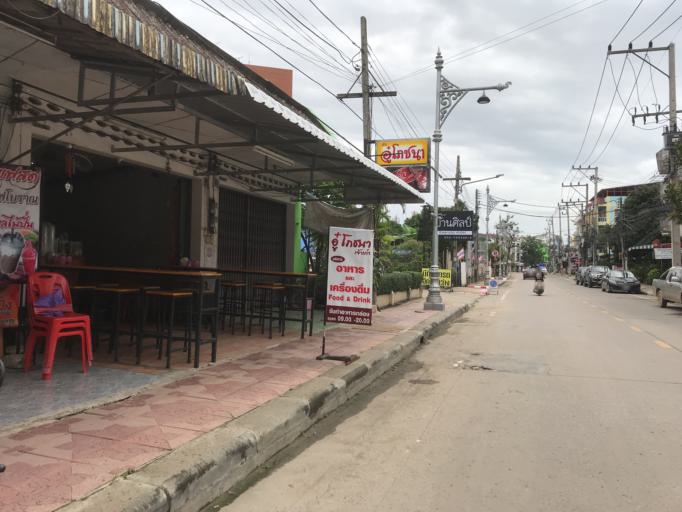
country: TH
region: Chiang Rai
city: Chiang Rai
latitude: 19.9020
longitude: 99.8257
